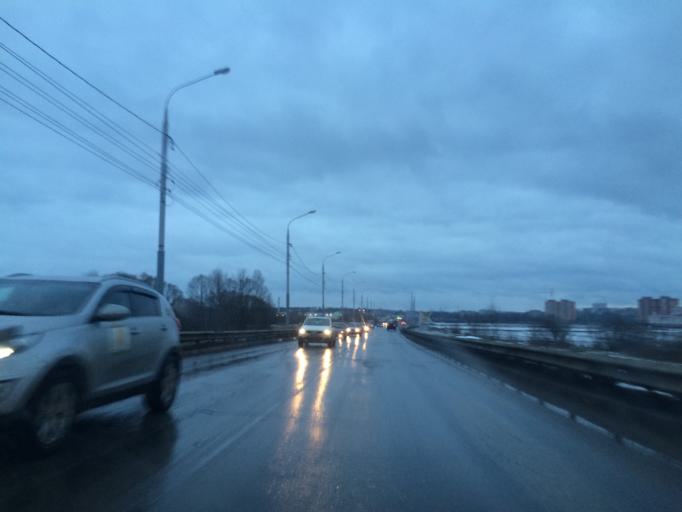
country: RU
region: Tula
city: Tula
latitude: 54.1906
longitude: 37.6568
